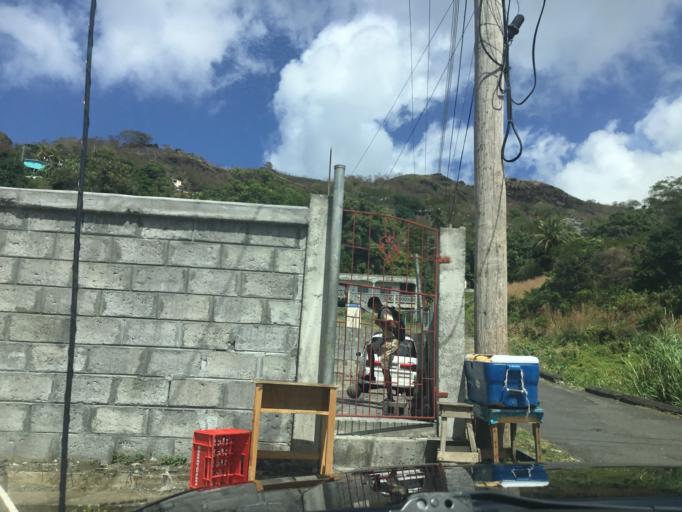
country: VC
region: Saint George
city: Kingstown Park
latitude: 13.1586
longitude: -61.2358
